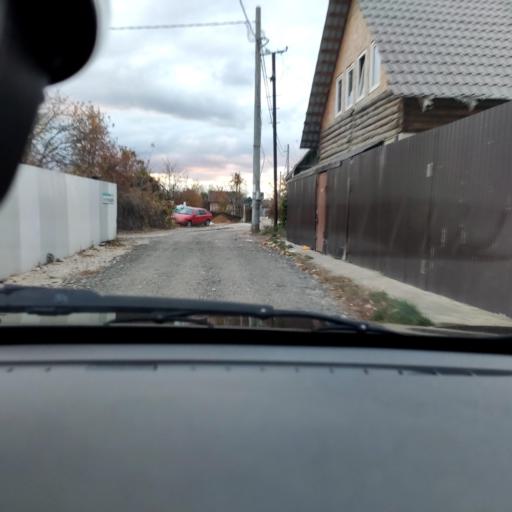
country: RU
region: Samara
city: Tol'yatti
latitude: 53.5394
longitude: 49.4287
